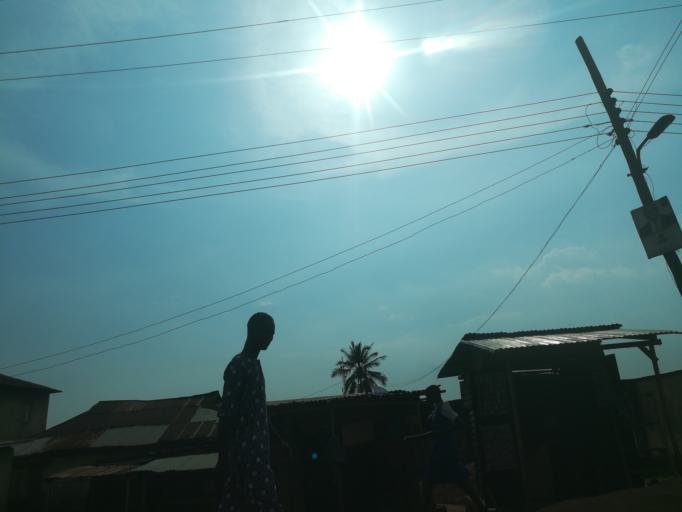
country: NG
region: Lagos
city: Ikorodu
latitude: 6.6674
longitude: 3.6712
